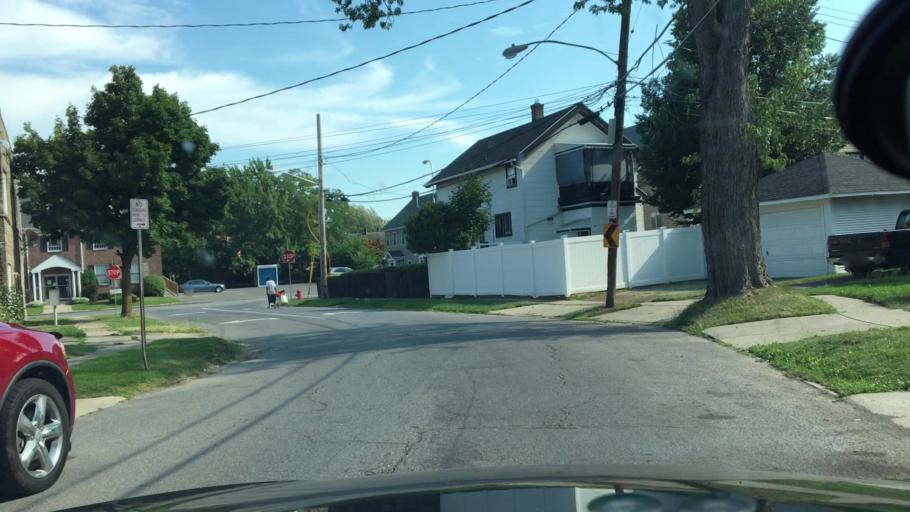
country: US
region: New York
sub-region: Erie County
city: Eggertsville
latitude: 42.9371
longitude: -78.8173
